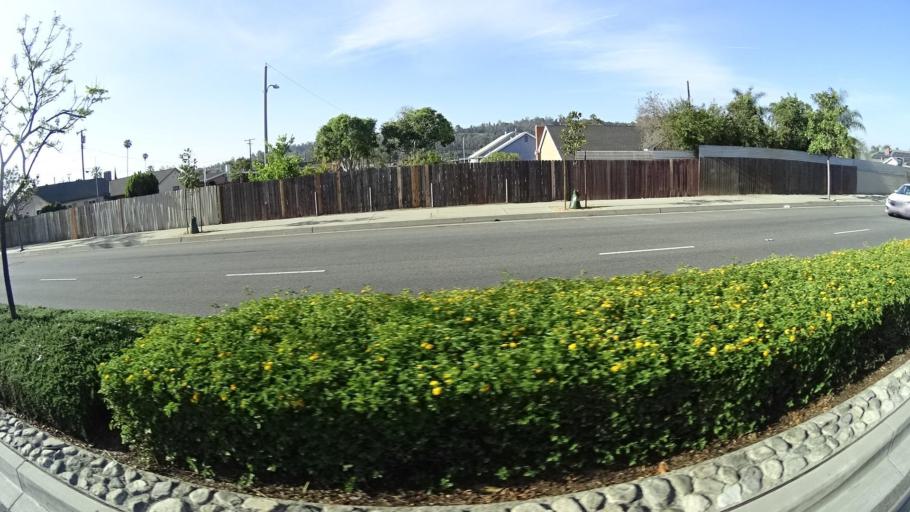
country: US
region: California
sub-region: Los Angeles County
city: Valinda
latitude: 34.0359
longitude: -117.9290
